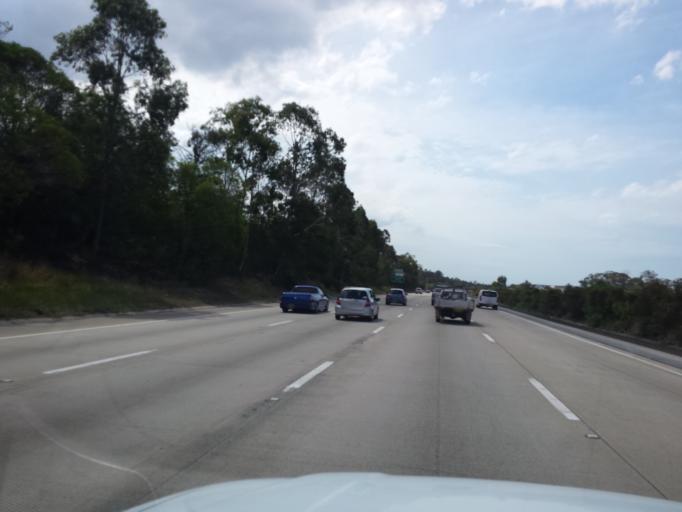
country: AU
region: Queensland
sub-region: Gold Coast
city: Nerang
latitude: -27.9460
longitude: 153.3397
